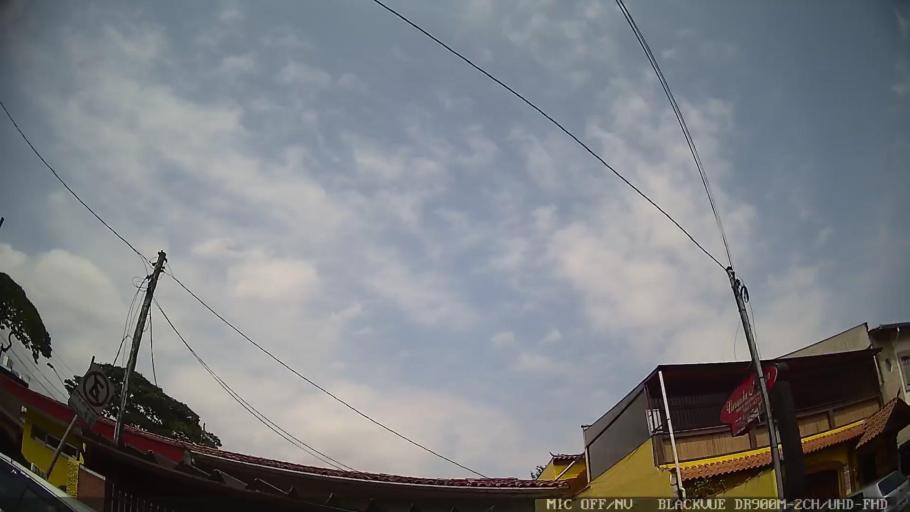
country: BR
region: Sao Paulo
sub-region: Taboao Da Serra
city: Taboao da Serra
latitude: -23.6467
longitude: -46.7227
